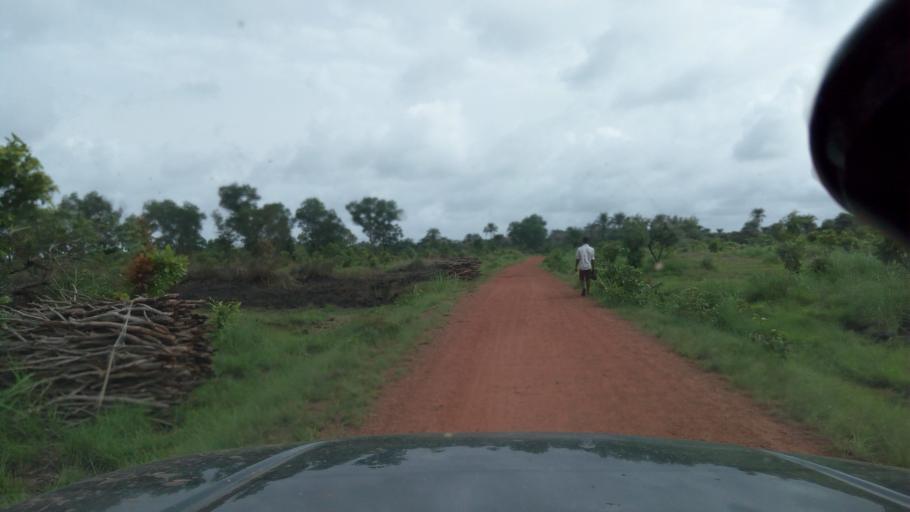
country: SL
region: Northern Province
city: Mange
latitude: 8.8258
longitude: -12.9320
